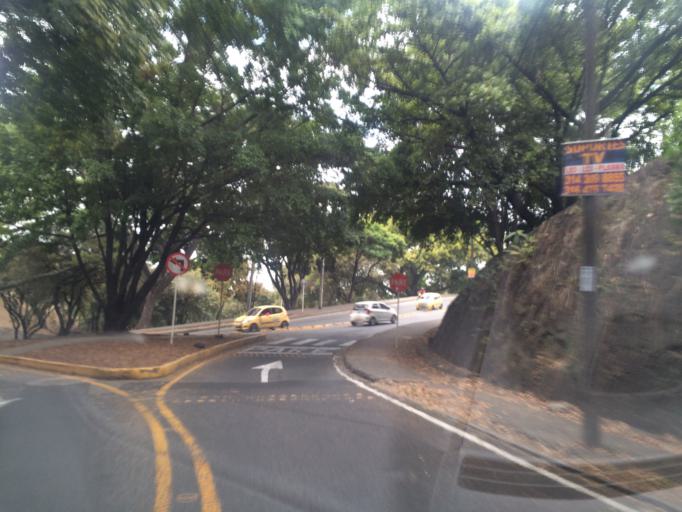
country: CO
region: Valle del Cauca
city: Cali
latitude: 3.4475
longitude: -76.5469
